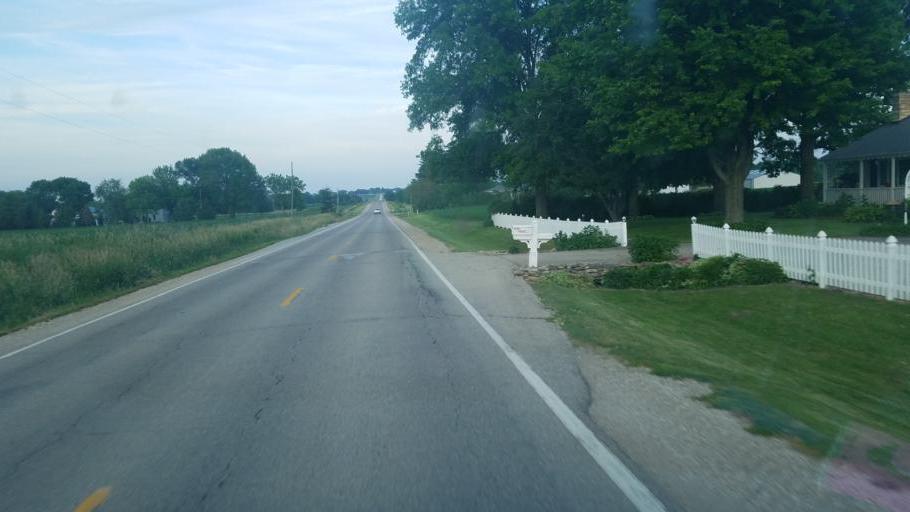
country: US
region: Iowa
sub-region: Benton County
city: Belle Plaine
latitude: 41.9061
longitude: -92.3126
